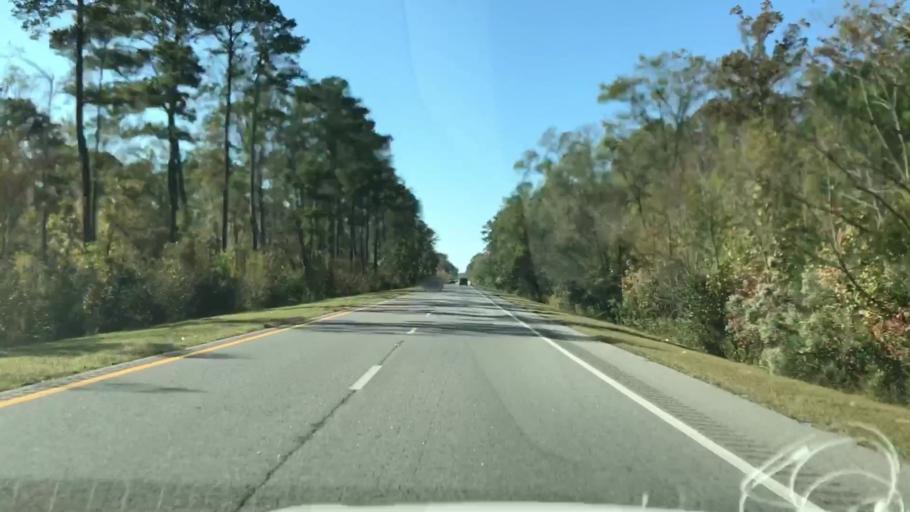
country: US
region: South Carolina
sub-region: Hampton County
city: Yemassee
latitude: 32.6427
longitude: -80.7091
